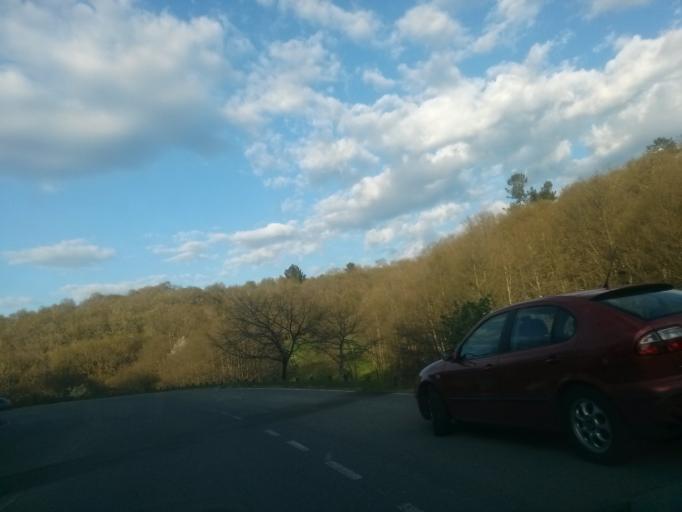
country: ES
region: Galicia
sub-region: Provincia de Lugo
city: Lugo
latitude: 42.9973
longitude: -7.5322
